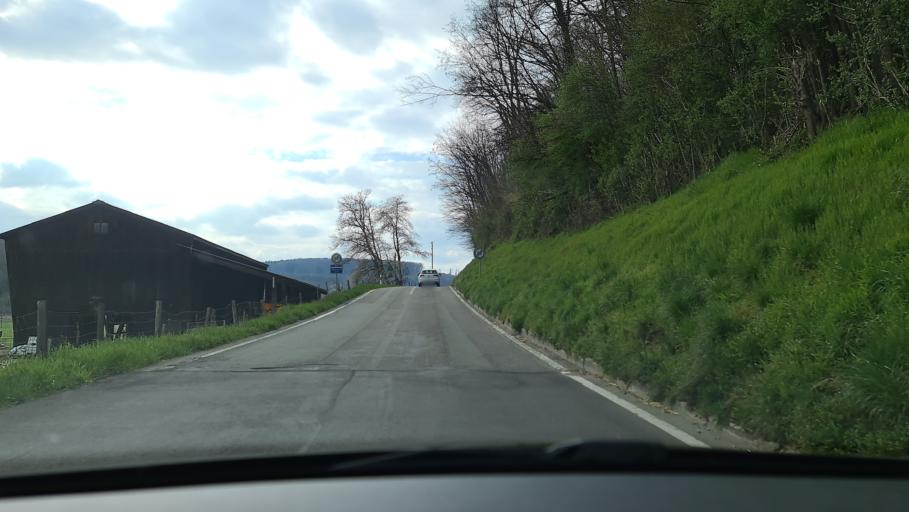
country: CH
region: Jura
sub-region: Porrentruy District
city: Boncourt
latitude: 47.4720
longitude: 7.0467
